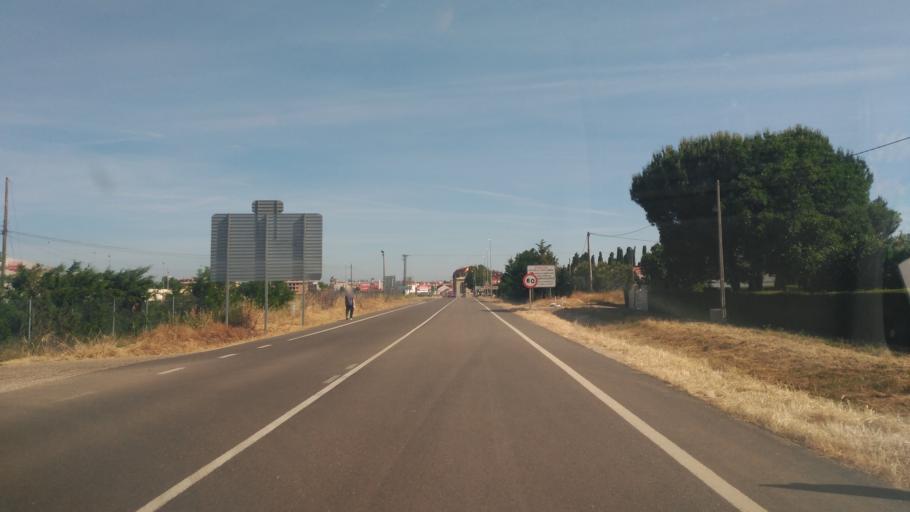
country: ES
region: Castille and Leon
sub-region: Provincia de Zamora
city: Zamora
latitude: 41.4865
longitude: -5.7433
